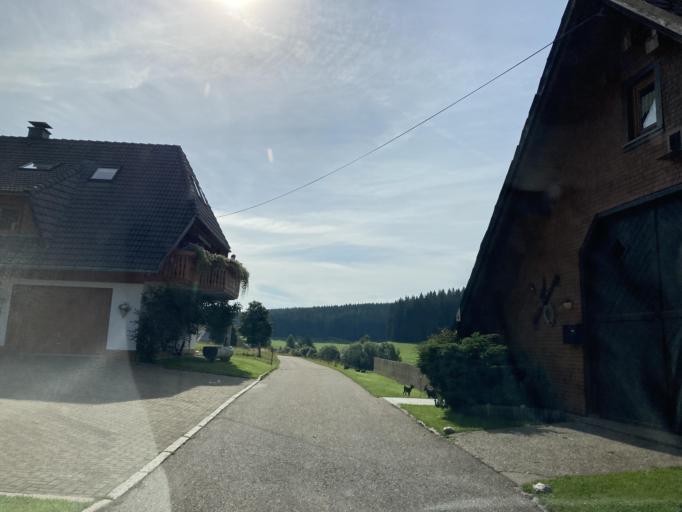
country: DE
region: Baden-Wuerttemberg
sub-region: Freiburg Region
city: Schonwald im Schwarzwald
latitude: 48.0970
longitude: 8.2193
